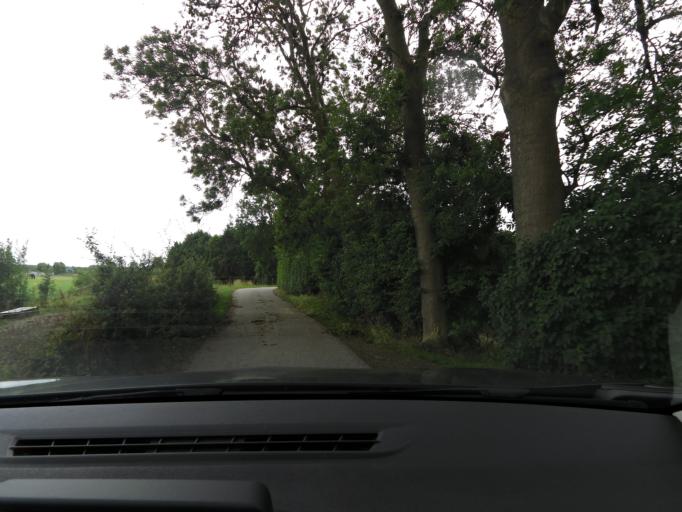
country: NL
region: South Holland
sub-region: Gemeente Hellevoetsluis
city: Nieuw-Helvoet
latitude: 51.8692
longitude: 4.0847
